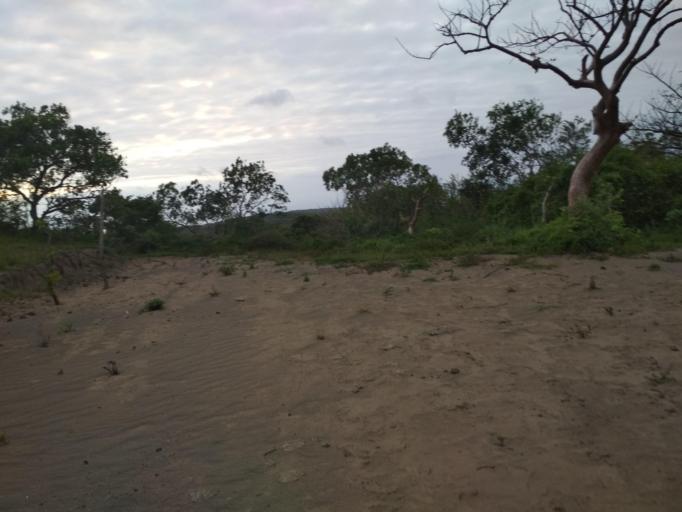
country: MX
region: Veracruz
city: Anton Lizardo
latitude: 19.0473
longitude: -95.9944
